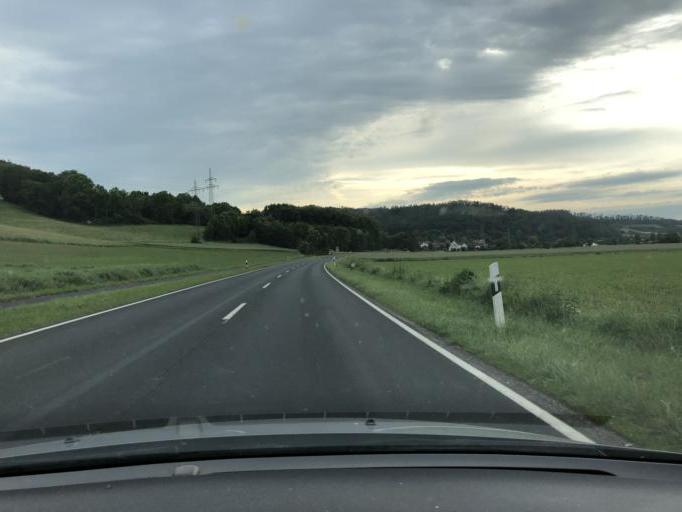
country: DE
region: Hesse
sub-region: Regierungsbezirk Kassel
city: Rotenburg an der Fulda
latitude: 51.0018
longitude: 9.7063
